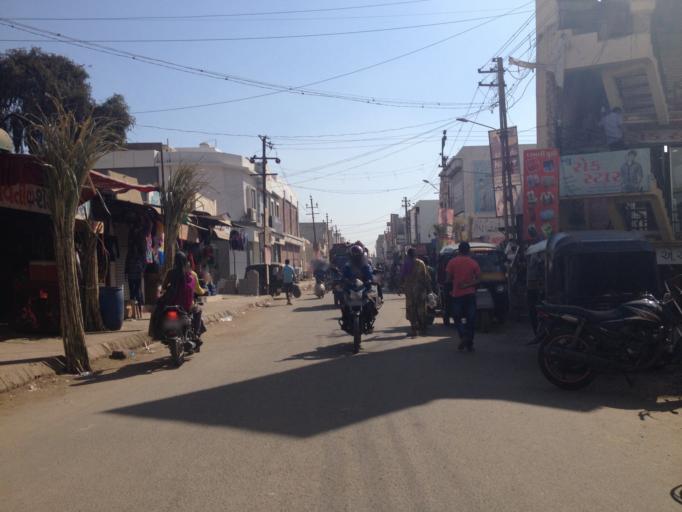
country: IN
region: Gujarat
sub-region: Kachchh
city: Anjar
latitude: 23.1125
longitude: 70.0282
